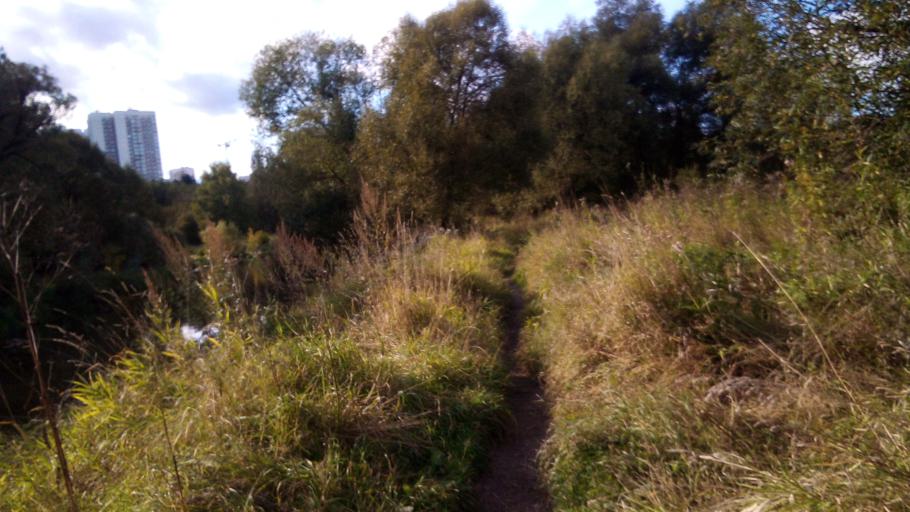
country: RU
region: Moscow
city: Strogino
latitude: 55.8438
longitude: 37.4127
